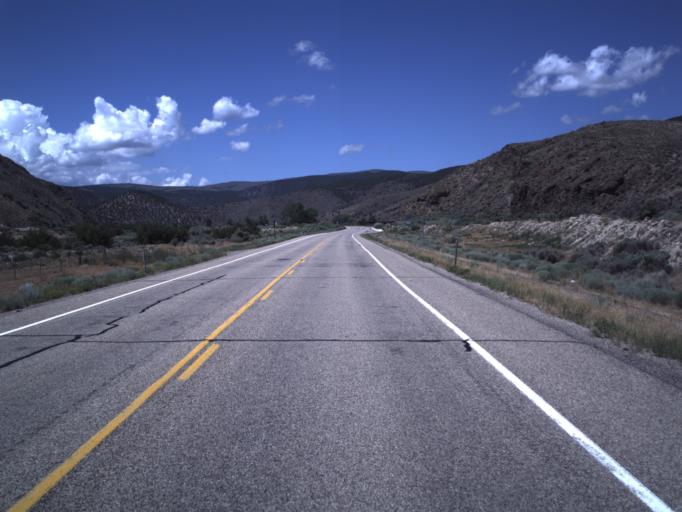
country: US
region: Utah
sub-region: Piute County
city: Junction
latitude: 38.1527
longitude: -112.2873
